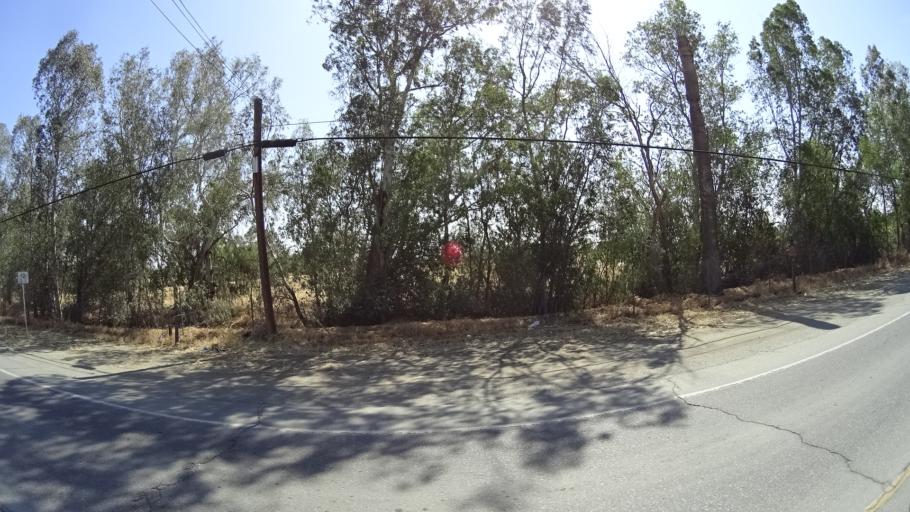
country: US
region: California
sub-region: Kings County
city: Home Garden
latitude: 36.3096
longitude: -119.6370
